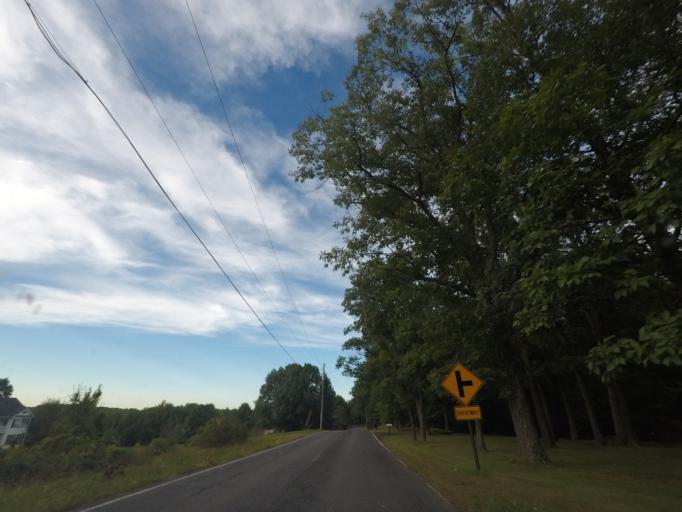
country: US
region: New York
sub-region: Rensselaer County
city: East Greenbush
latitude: 42.6079
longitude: -73.6762
